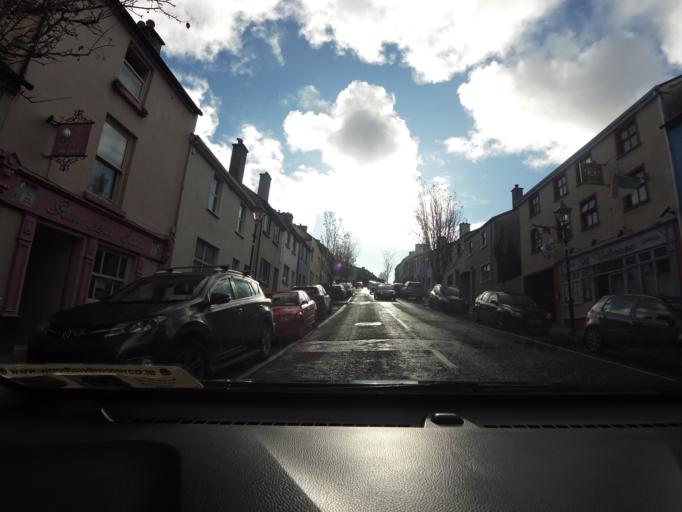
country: IE
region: Connaught
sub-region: Maigh Eo
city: Westport
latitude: 53.7979
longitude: -9.5229
